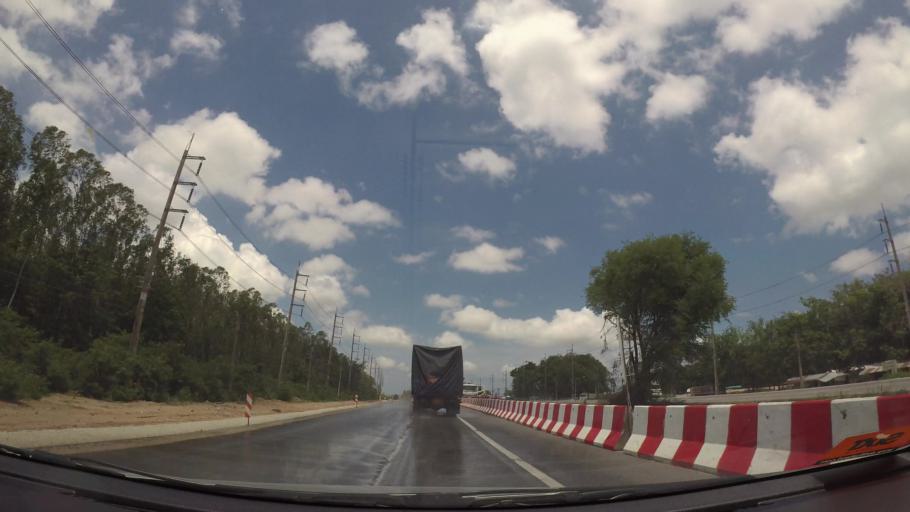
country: TH
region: Rayong
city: Nikhom Phattana
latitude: 12.7901
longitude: 101.1558
